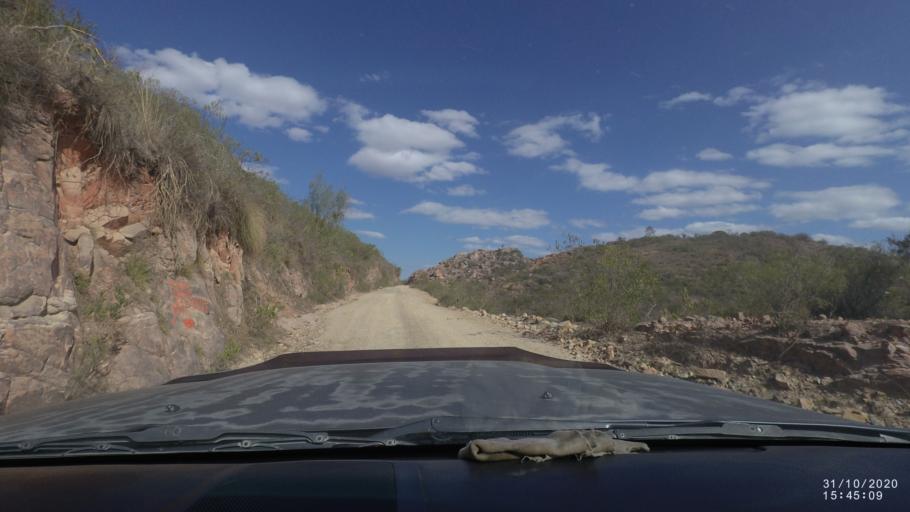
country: BO
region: Chuquisaca
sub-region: Provincia Zudanez
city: Mojocoya
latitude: -18.3186
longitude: -64.7186
